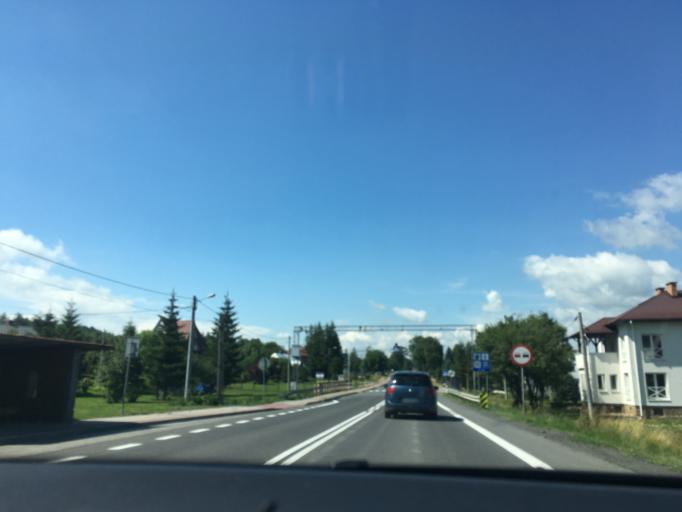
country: PL
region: Subcarpathian Voivodeship
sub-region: Powiat krosnienski
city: Dukla
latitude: 49.5400
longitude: 21.6929
